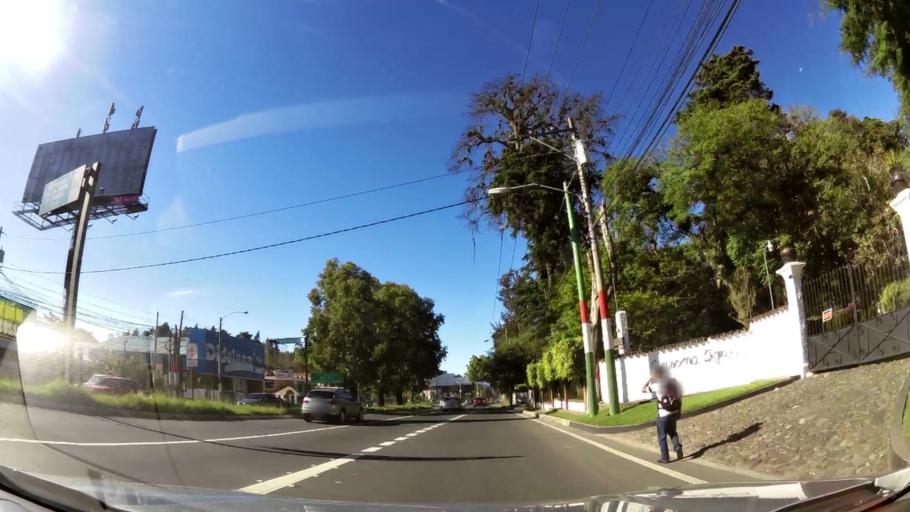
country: GT
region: Guatemala
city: San Jose Pinula
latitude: 14.5377
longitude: -90.4556
